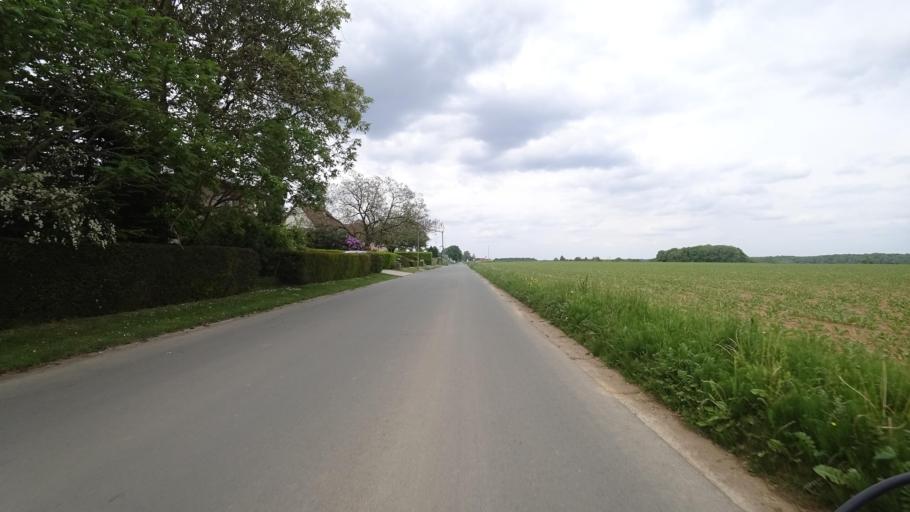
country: BE
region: Wallonia
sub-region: Province du Brabant Wallon
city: Grez-Doiceau
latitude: 50.6989
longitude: 4.6752
